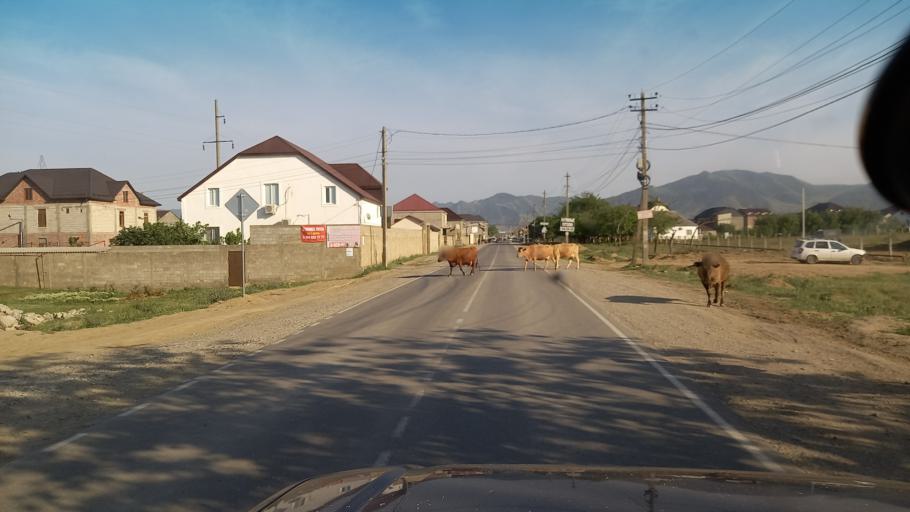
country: RU
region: Dagestan
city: Shamkhal-Termen
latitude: 43.0103
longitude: 47.3308
